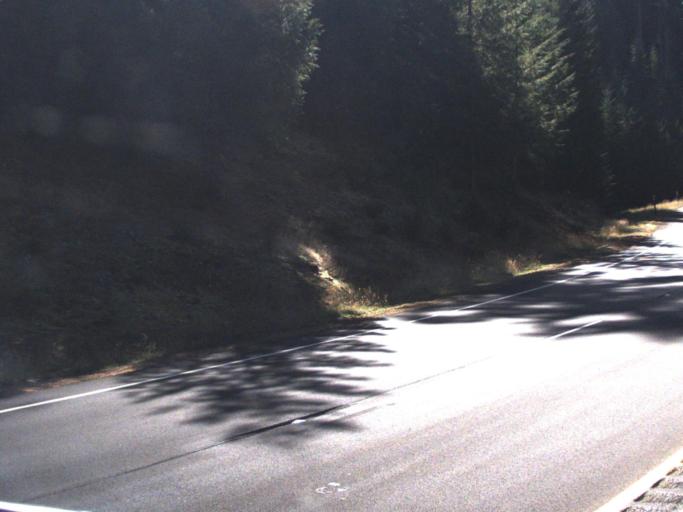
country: US
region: Washington
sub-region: Pierce County
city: Buckley
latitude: 46.6954
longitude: -121.5688
